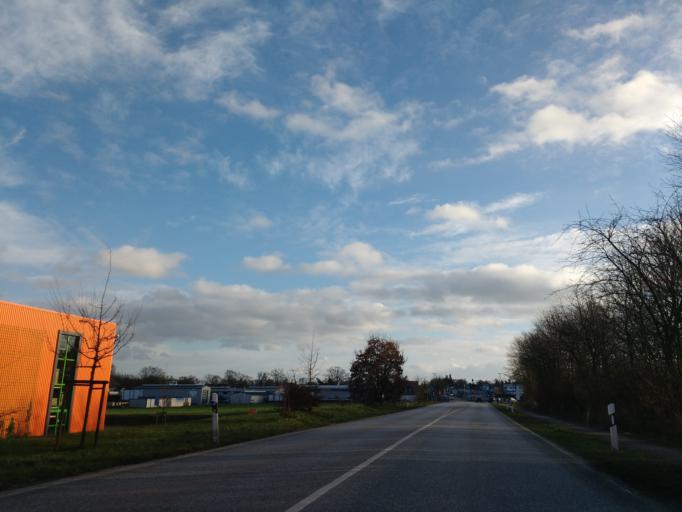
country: DE
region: Schleswig-Holstein
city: Kaltenkirchen
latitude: 53.8434
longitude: 9.9436
